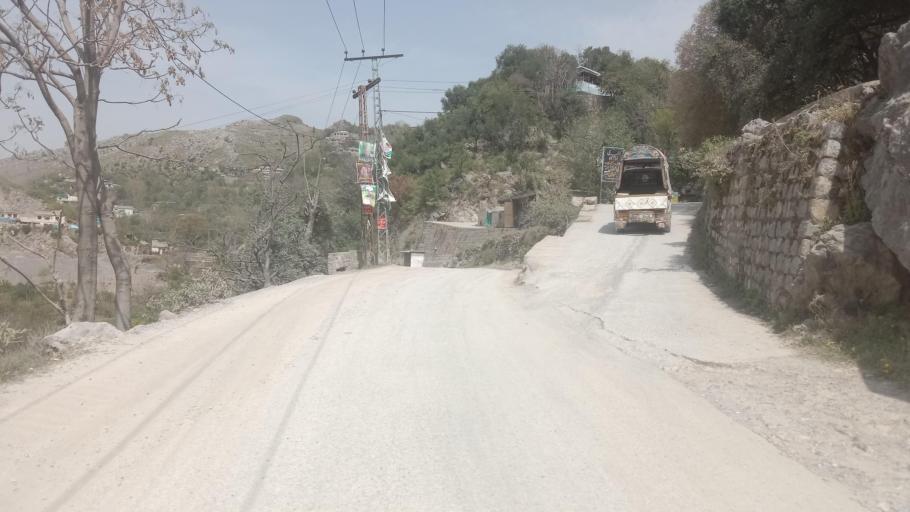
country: PK
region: Khyber Pakhtunkhwa
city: Abbottabad
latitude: 34.1629
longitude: 73.2821
